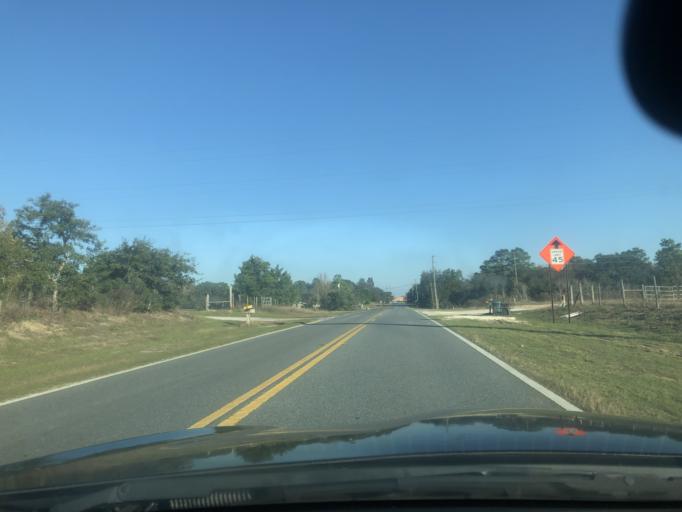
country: US
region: Florida
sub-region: Citrus County
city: Sugarmill Woods
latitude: 28.7640
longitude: -82.5177
